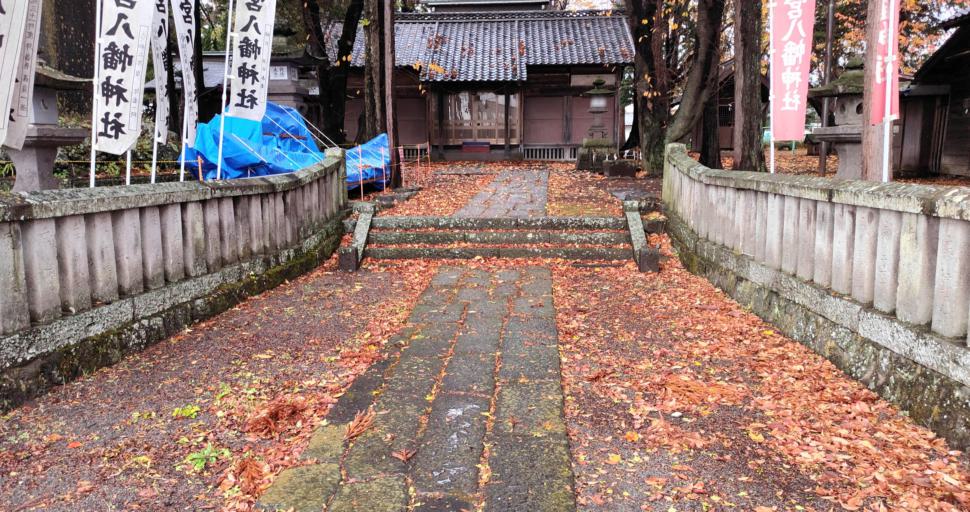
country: JP
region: Nagano
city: Saku
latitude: 36.2697
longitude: 138.4737
